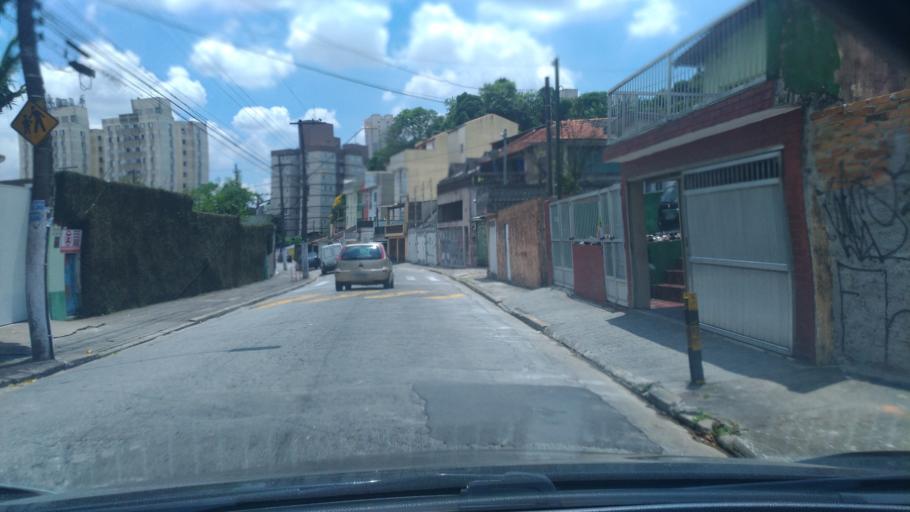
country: BR
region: Sao Paulo
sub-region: Santo Andre
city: Santo Andre
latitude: -23.6959
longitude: -46.5046
